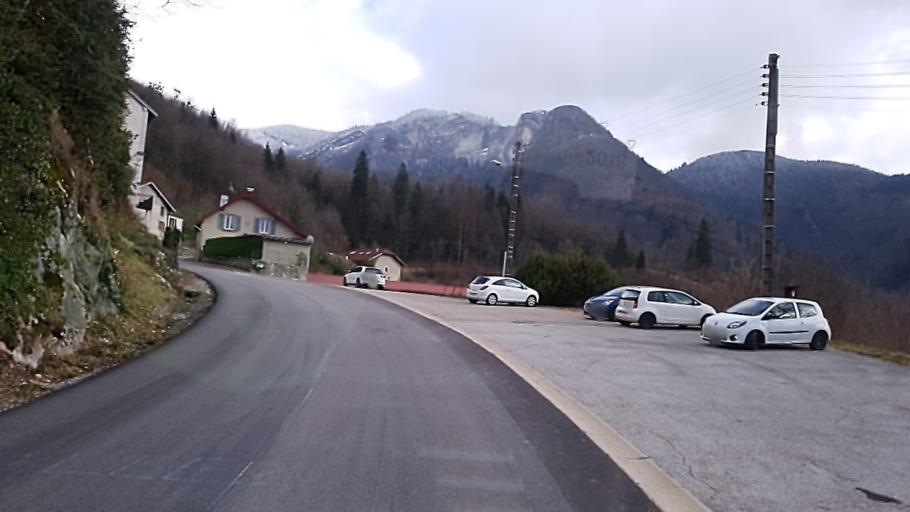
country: FR
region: Franche-Comte
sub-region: Departement du Jura
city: Saint-Claude
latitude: 46.3675
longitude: 5.8827
